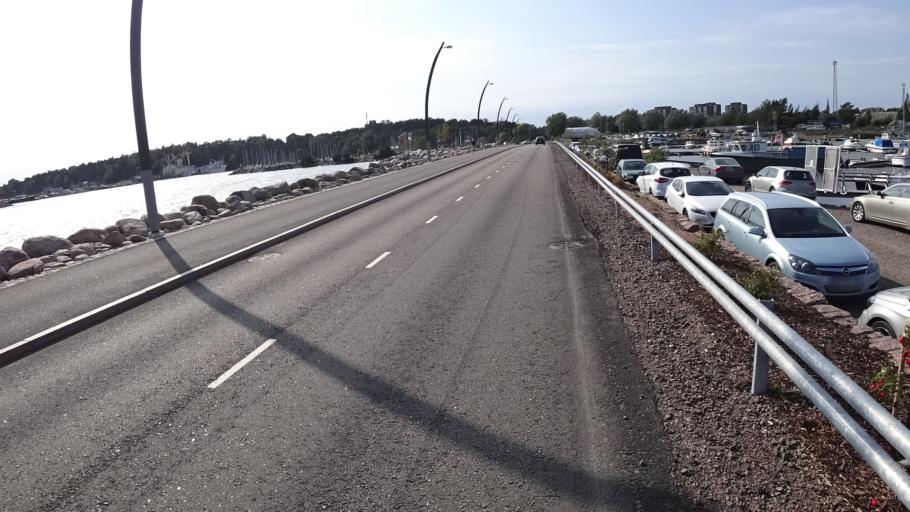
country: FI
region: Kymenlaakso
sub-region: Kotka-Hamina
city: Kotka
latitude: 60.4588
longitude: 26.9598
